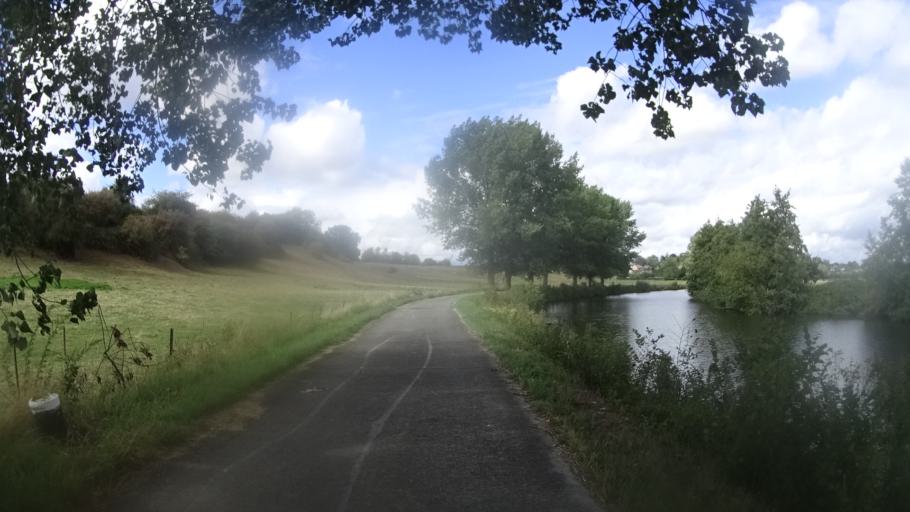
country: BE
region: Wallonia
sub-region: Province du Hainaut
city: Merbes-le-Chateau
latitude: 50.3157
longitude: 4.1500
